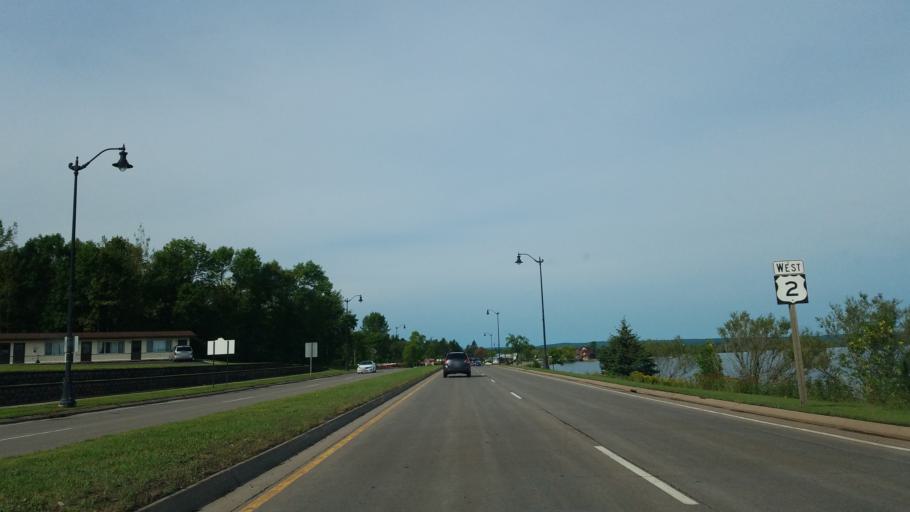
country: US
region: Wisconsin
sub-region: Ashland County
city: Ashland
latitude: 46.5829
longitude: -90.9070
